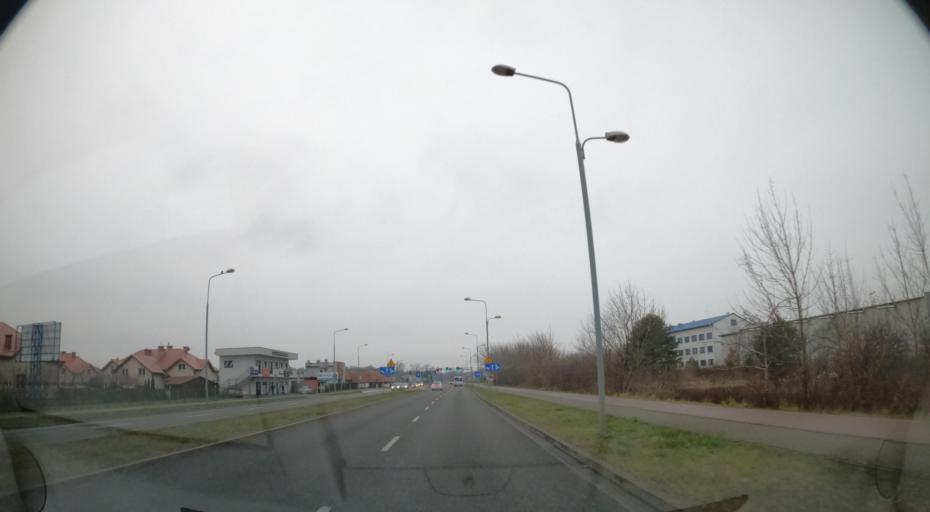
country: PL
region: Masovian Voivodeship
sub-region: Radom
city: Radom
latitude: 51.4189
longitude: 21.2076
